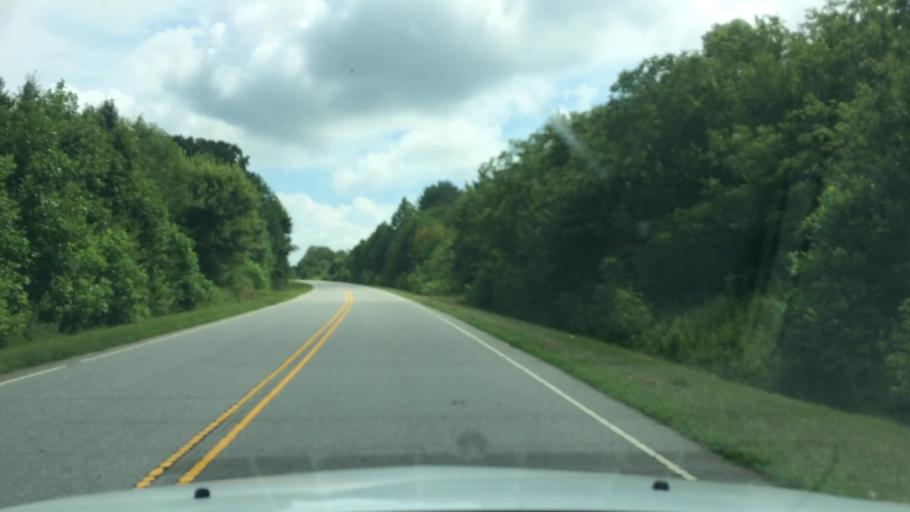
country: US
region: North Carolina
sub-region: Yadkin County
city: Jonesville
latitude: 36.1231
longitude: -80.8487
